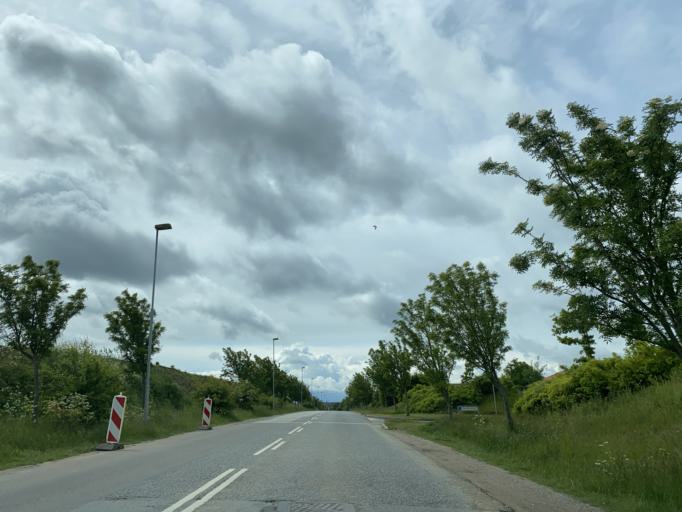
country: DK
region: Central Jutland
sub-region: Arhus Kommune
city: Stavtrup
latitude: 56.1916
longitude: 10.1311
